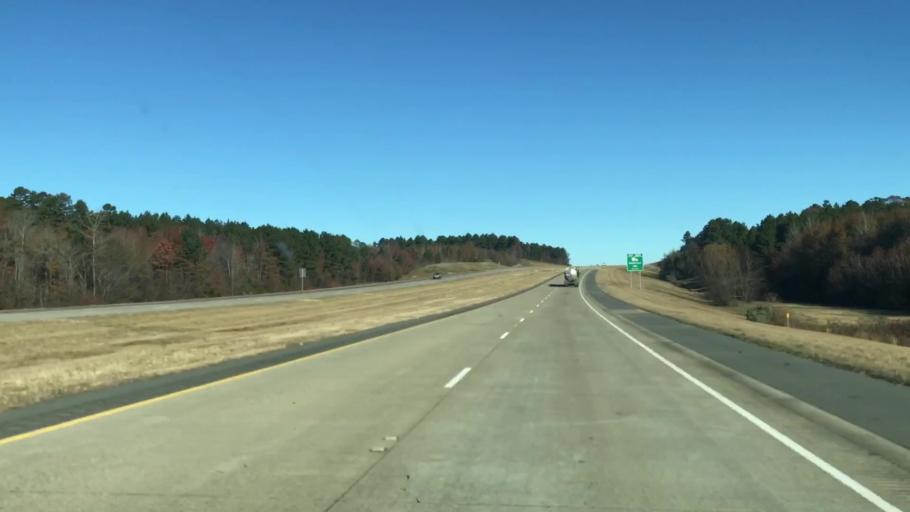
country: US
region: Louisiana
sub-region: Caddo Parish
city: Vivian
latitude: 32.9839
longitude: -93.9105
